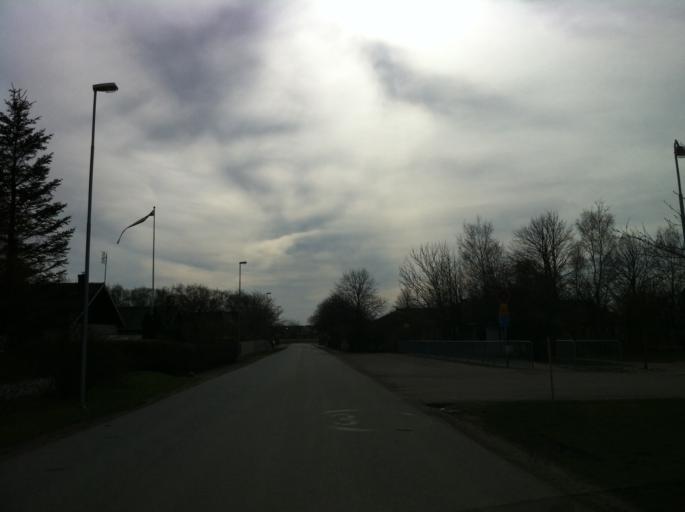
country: SE
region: Skane
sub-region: Hoganas Kommun
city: Hoganas
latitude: 56.2439
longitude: 12.5426
